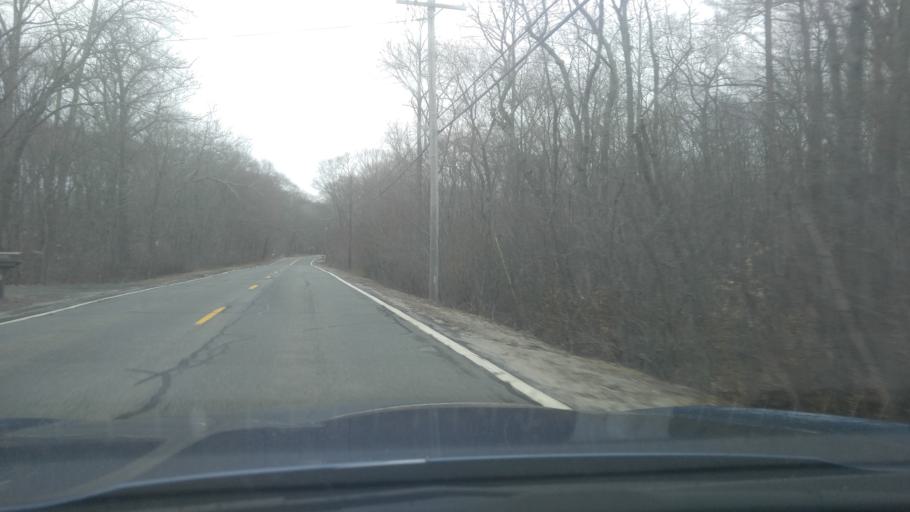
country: US
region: Rhode Island
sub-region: Kent County
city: Coventry
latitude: 41.6766
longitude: -71.6526
